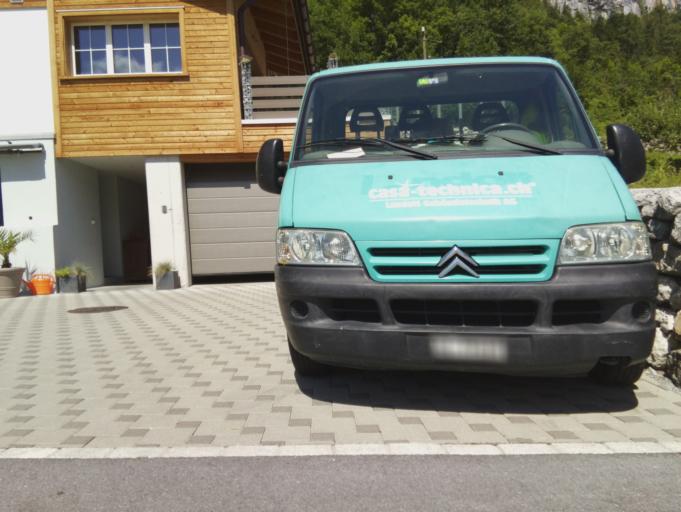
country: CH
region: Glarus
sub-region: Glarus
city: Nafels
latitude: 47.0964
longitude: 9.0577
